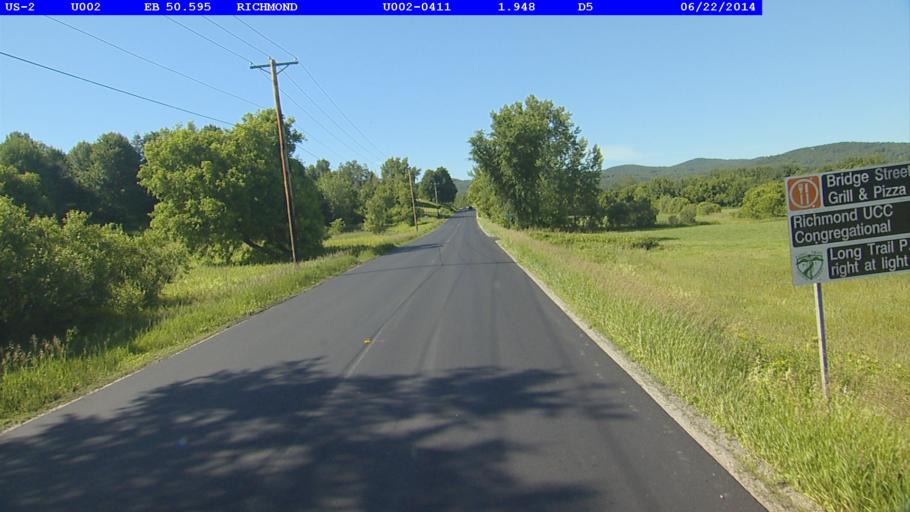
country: US
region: Vermont
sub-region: Chittenden County
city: Williston
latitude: 44.4144
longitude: -72.9991
